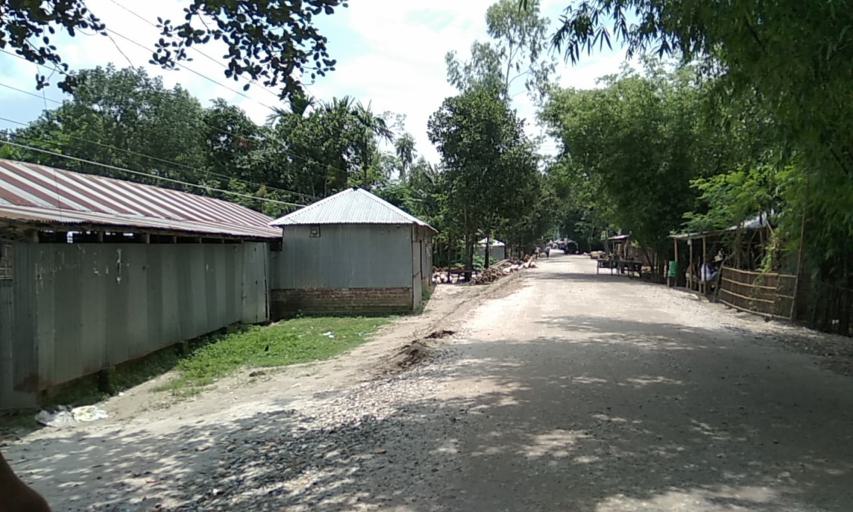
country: BD
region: Rangpur Division
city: Rangpur
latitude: 25.8879
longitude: 89.1846
